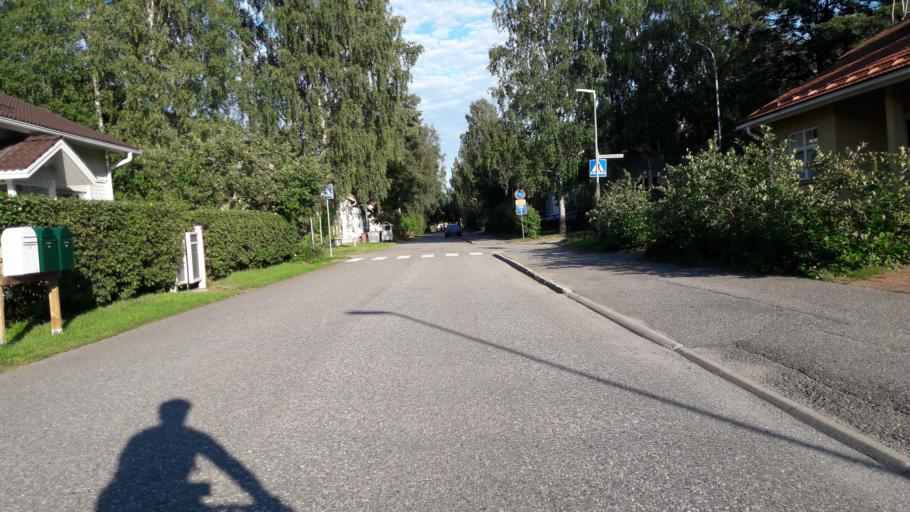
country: FI
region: North Karelia
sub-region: Joensuu
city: Joensuu
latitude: 62.6093
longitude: 29.7586
